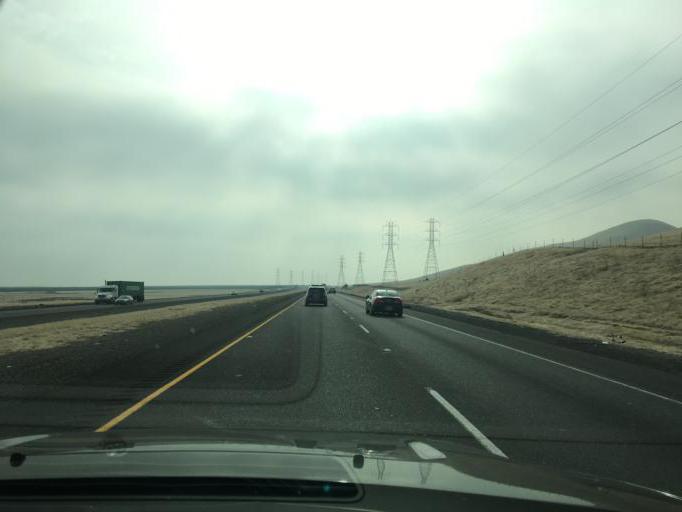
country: US
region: California
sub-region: Merced County
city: Los Banos
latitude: 36.8961
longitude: -120.8071
